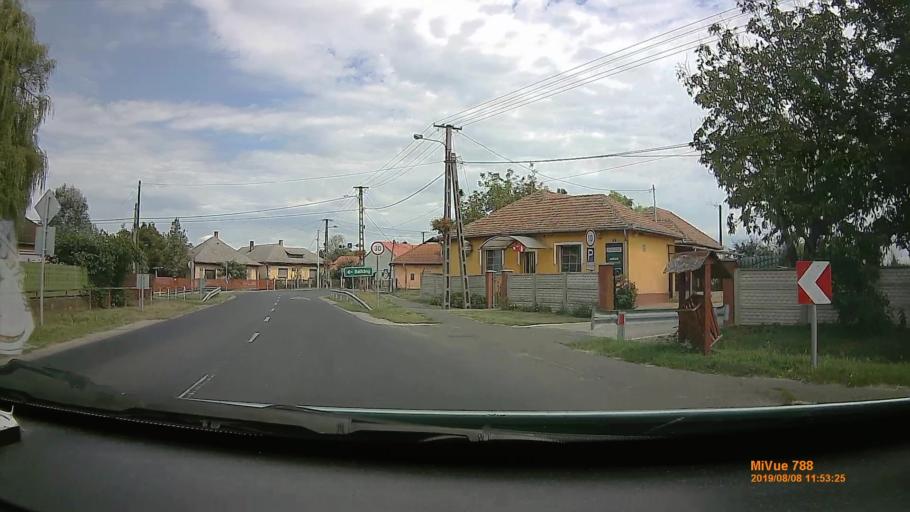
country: HU
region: Szabolcs-Szatmar-Bereg
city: Nyirmihalydi
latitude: 47.7322
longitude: 21.9611
